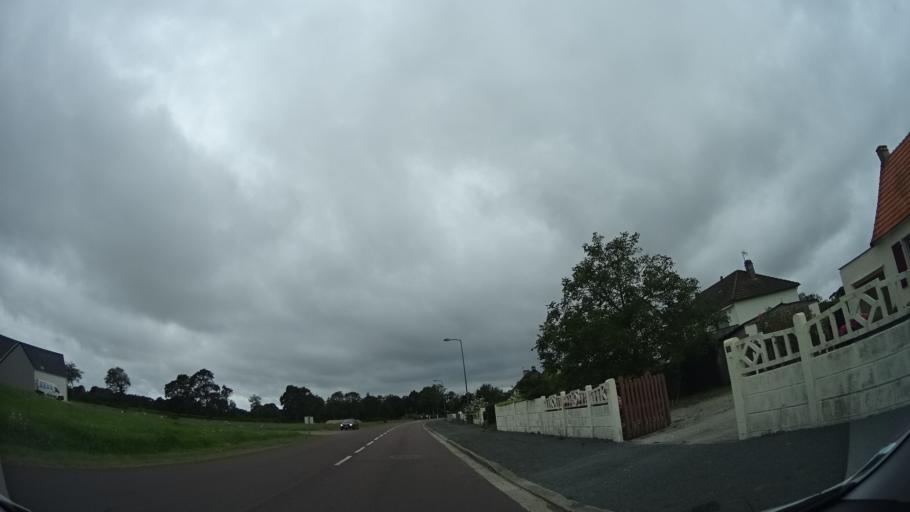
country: FR
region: Lower Normandy
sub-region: Departement de la Manche
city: La Haye-du-Puits
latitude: 49.3013
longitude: -1.5781
